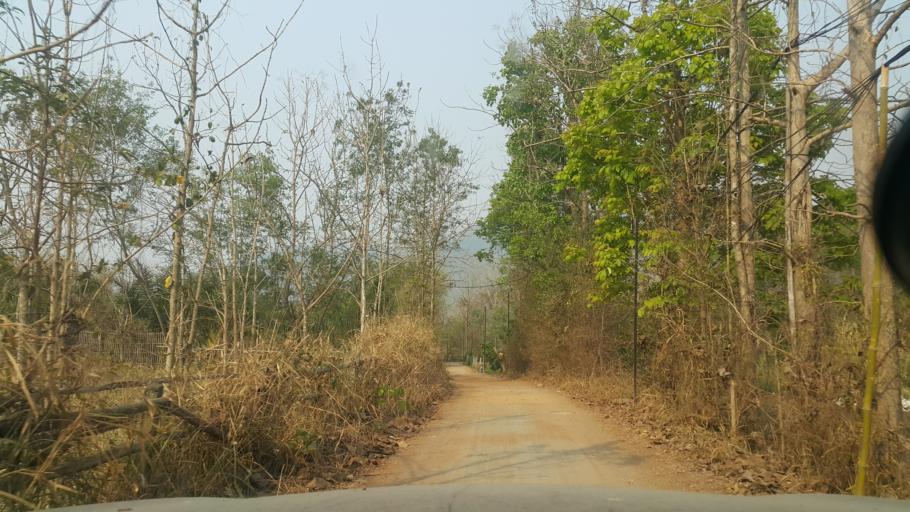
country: TH
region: Chiang Mai
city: Mae On
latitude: 18.7677
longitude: 99.2679
